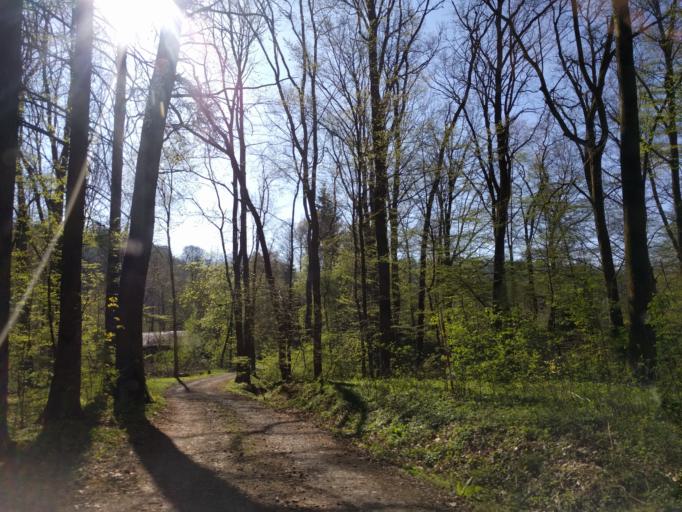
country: CZ
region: Central Bohemia
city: Kostelec nad Cernymi Lesy
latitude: 50.0260
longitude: 14.8152
